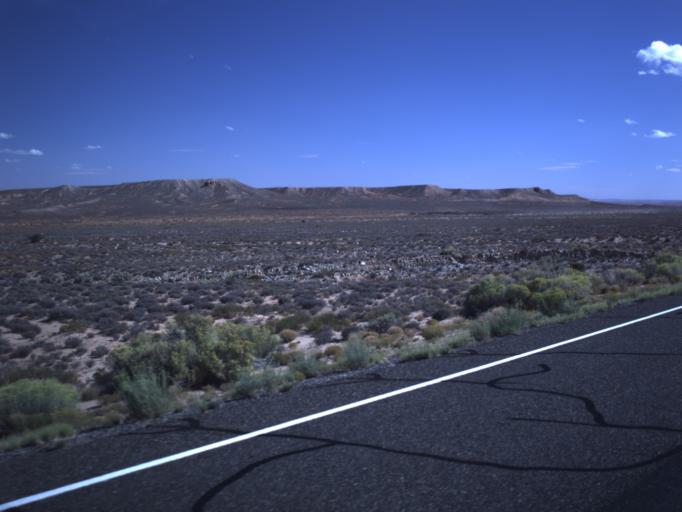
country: US
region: Utah
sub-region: Wayne County
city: Loa
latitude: 38.1106
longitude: -110.6246
